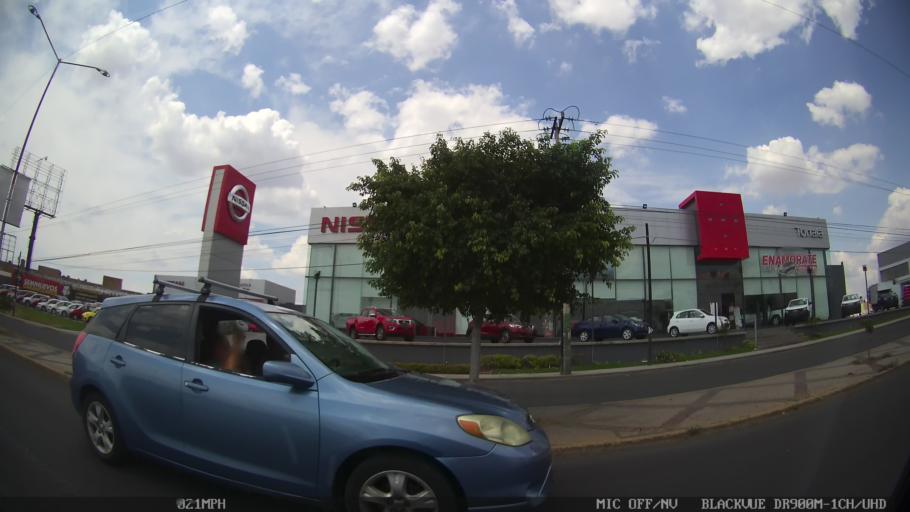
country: MX
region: Jalisco
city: Tlaquepaque
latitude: 20.6377
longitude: -103.2748
